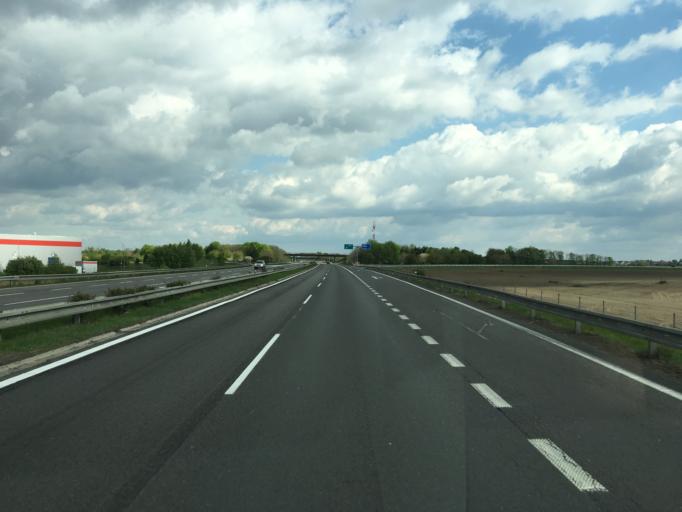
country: SK
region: Bratislavsky
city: Stupava
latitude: 48.3227
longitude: 17.0232
